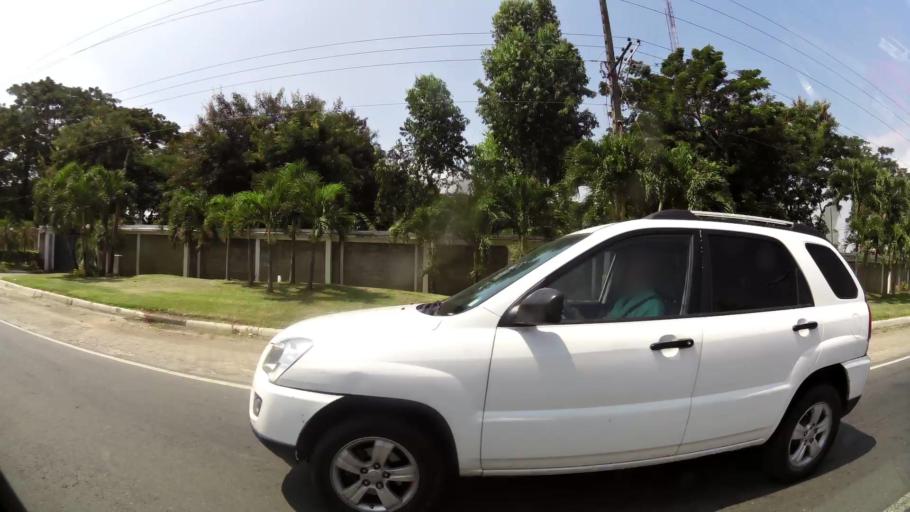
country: EC
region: Guayas
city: Eloy Alfaro
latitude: -2.1112
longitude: -79.8712
